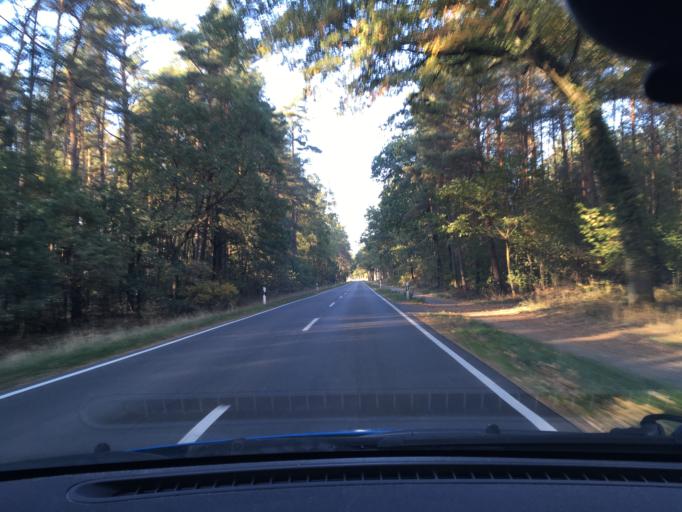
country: DE
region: Lower Saxony
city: Neu Darchau
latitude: 53.2604
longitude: 10.9566
